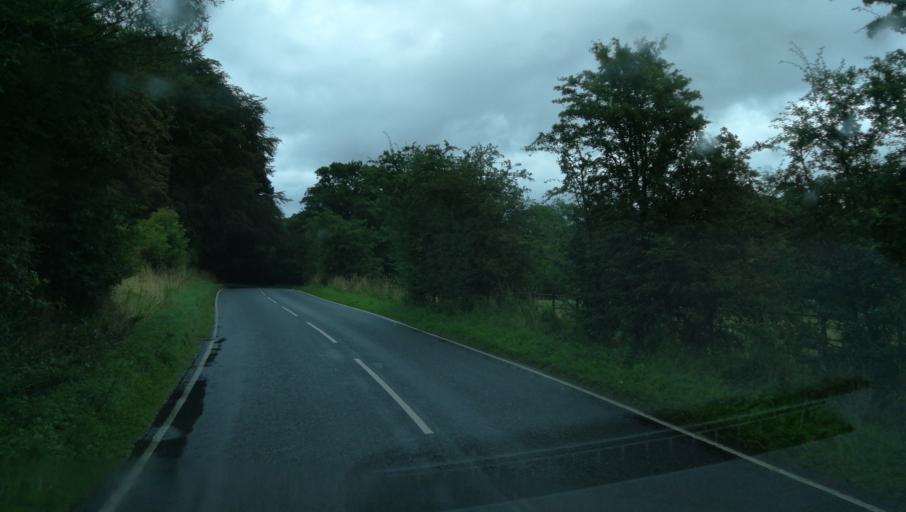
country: GB
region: England
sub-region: Cumbria
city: Penrith
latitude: 54.6238
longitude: -2.8161
